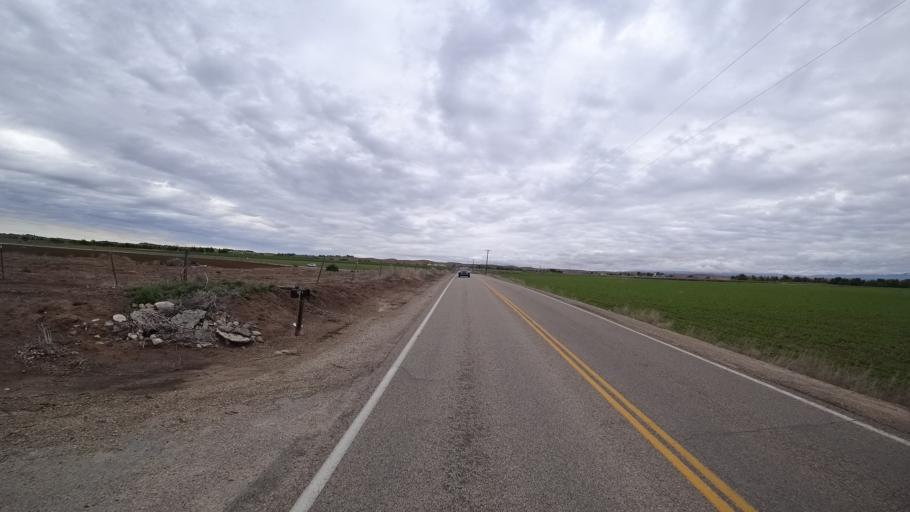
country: US
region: Idaho
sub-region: Ada County
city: Star
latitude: 43.7089
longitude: -116.4434
